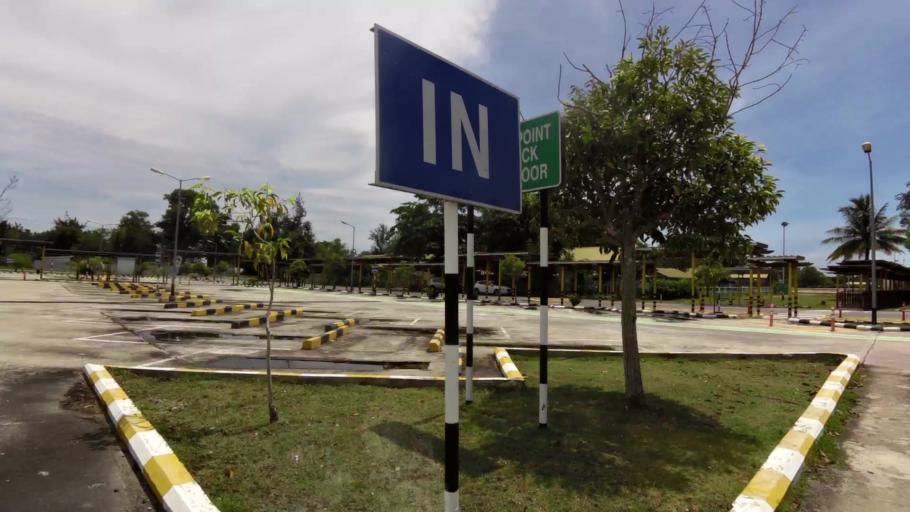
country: BN
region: Belait
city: Seria
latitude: 4.6068
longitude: 114.2950
